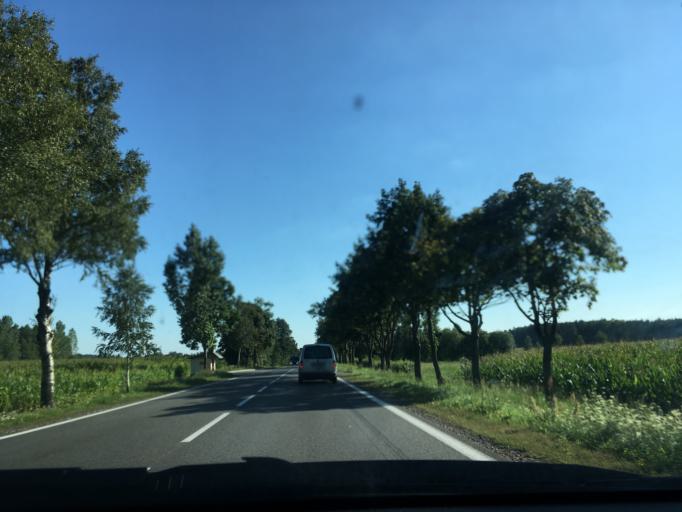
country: PL
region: Podlasie
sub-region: Powiat sokolski
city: Janow
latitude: 53.4085
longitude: 23.1179
